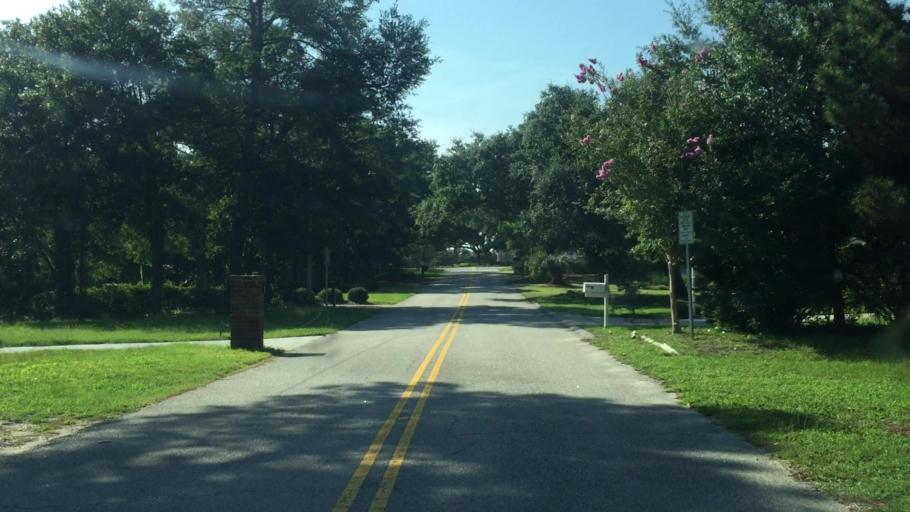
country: US
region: South Carolina
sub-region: Horry County
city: Myrtle Beach
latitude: 33.7452
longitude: -78.8133
